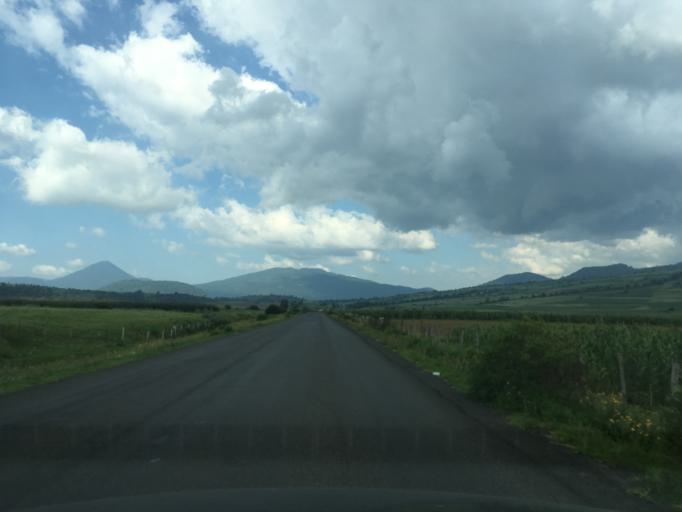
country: MX
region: Michoacan
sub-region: Nahuatzen
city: Comachuen
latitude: 19.6008
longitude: -101.9541
